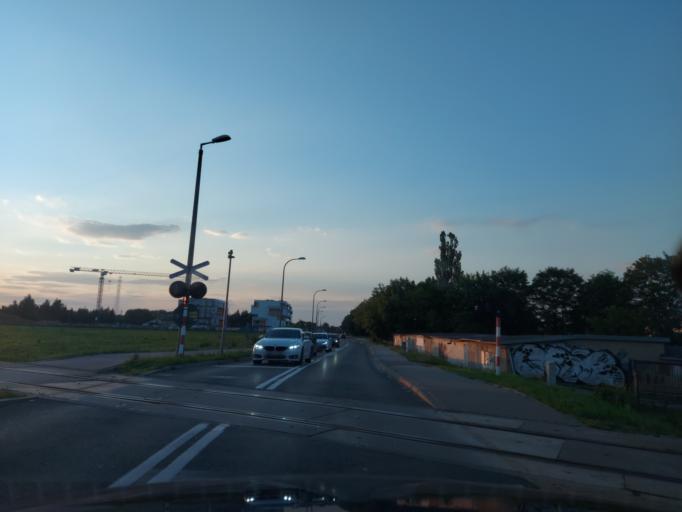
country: PL
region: Masovian Voivodeship
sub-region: Powiat piaseczynski
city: Piaseczno
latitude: 52.0851
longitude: 21.0141
